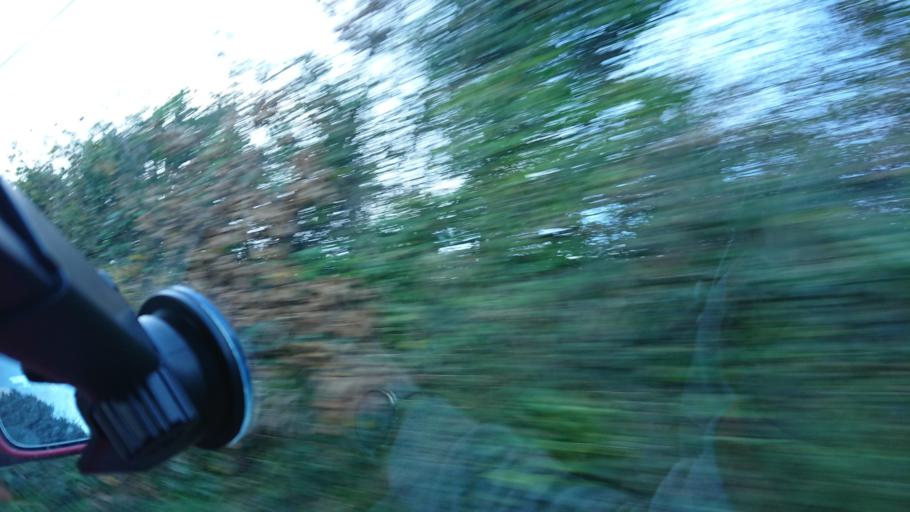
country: GB
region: England
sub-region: Cornwall
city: Looe
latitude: 50.3467
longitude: -4.4747
